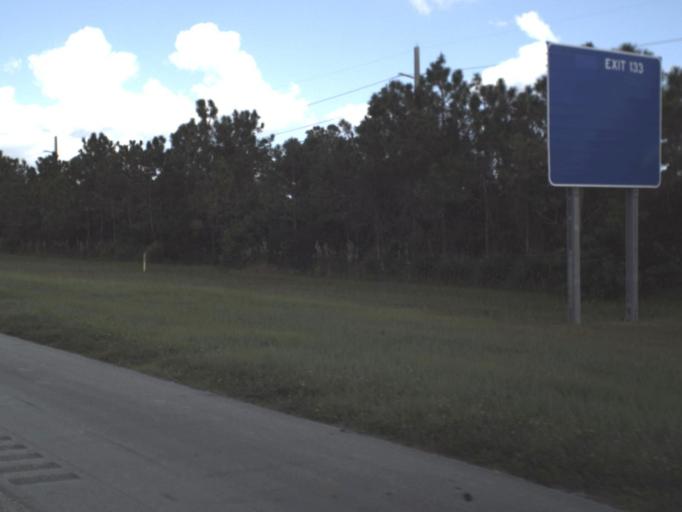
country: US
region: Florida
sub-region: Martin County
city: Palm City
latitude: 27.1468
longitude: -80.2946
